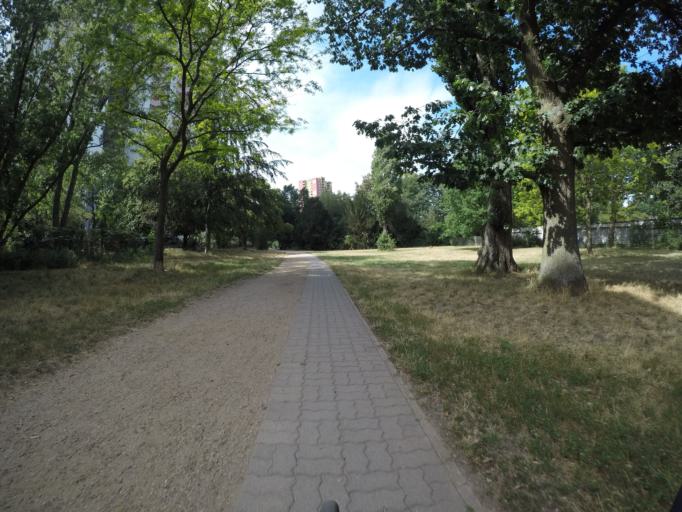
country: DE
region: Berlin
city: Marienfelde
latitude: 52.4096
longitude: 13.3526
